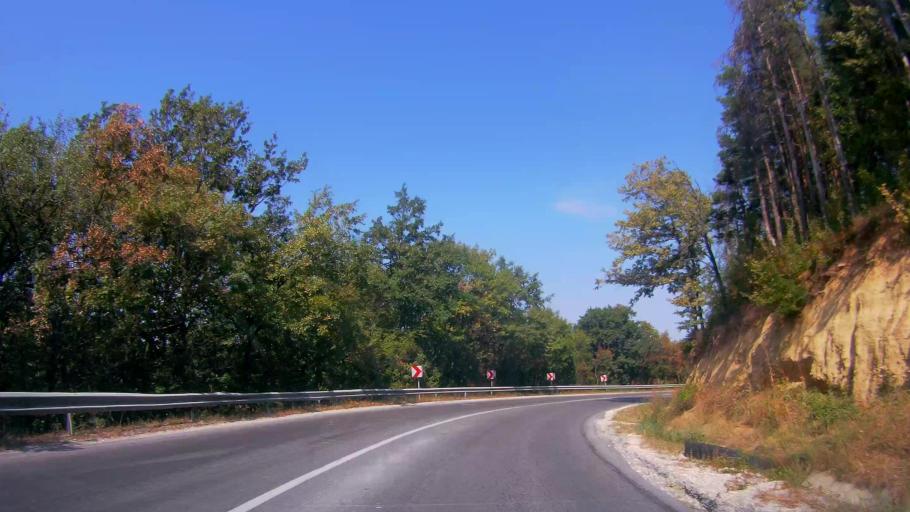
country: BG
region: Shumen
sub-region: Obshtina Smyadovo
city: Smyadovo
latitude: 42.9472
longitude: 26.9363
